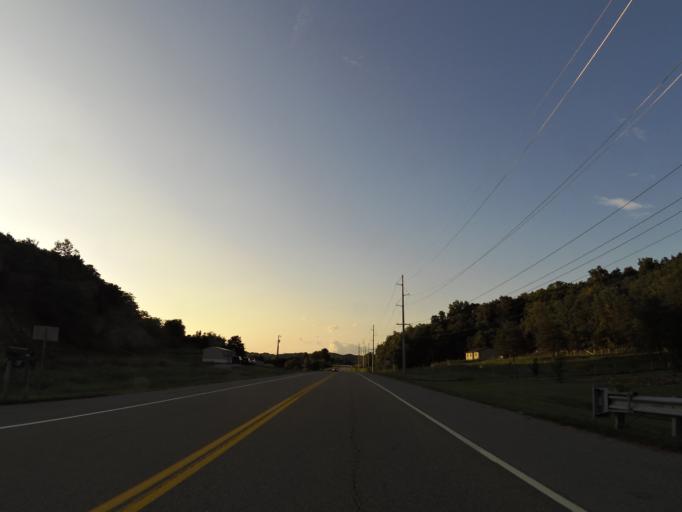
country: US
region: Tennessee
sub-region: Grainger County
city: Blaine
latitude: 36.1646
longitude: -83.7368
